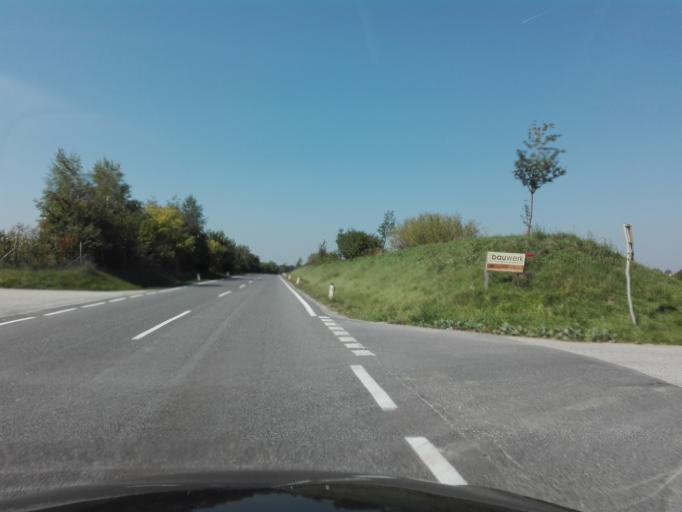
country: AT
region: Upper Austria
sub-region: Politischer Bezirk Linz-Land
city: Horsching
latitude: 48.2199
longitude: 14.1740
